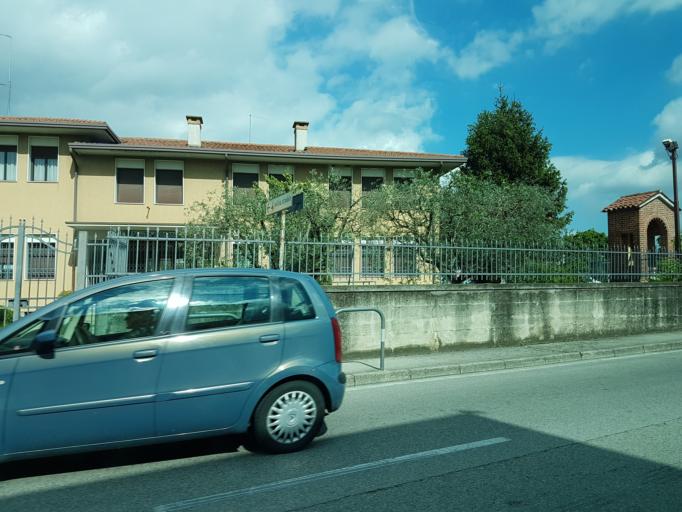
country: IT
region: Veneto
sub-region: Provincia di Vicenza
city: Bassano del Grappa
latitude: 45.7578
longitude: 11.7423
